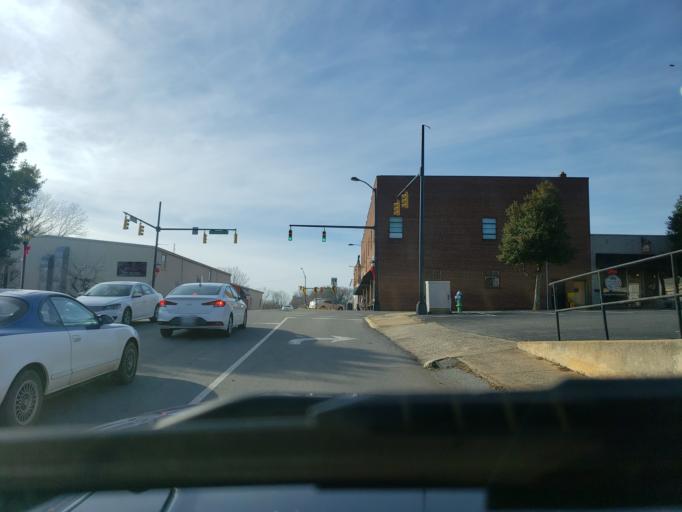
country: US
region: North Carolina
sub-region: Cleveland County
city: Kings Mountain
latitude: 35.2377
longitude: -81.3431
